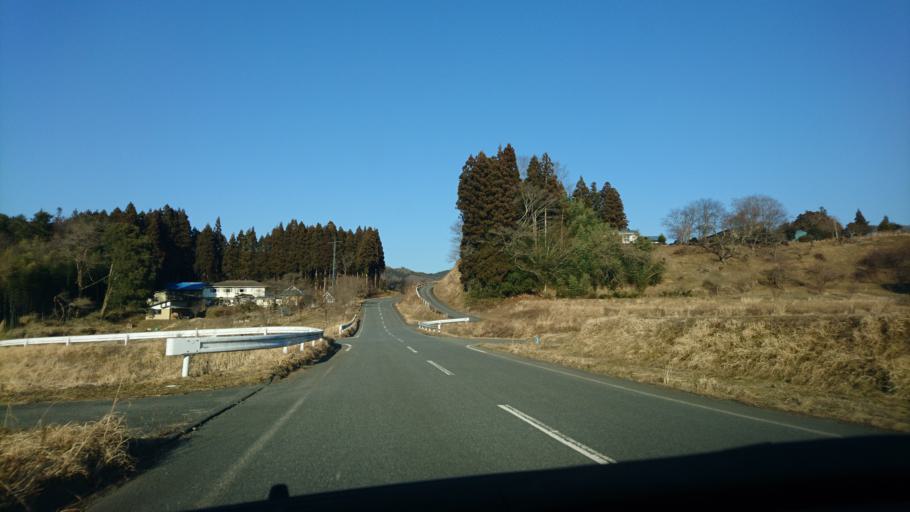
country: JP
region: Iwate
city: Ichinoseki
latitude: 38.8409
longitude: 141.3812
